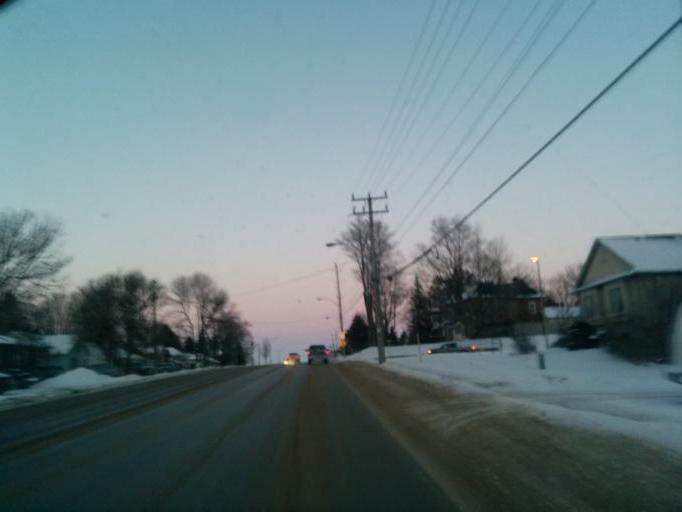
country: CA
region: Ontario
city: Shelburne
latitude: 44.0805
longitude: -80.1938
